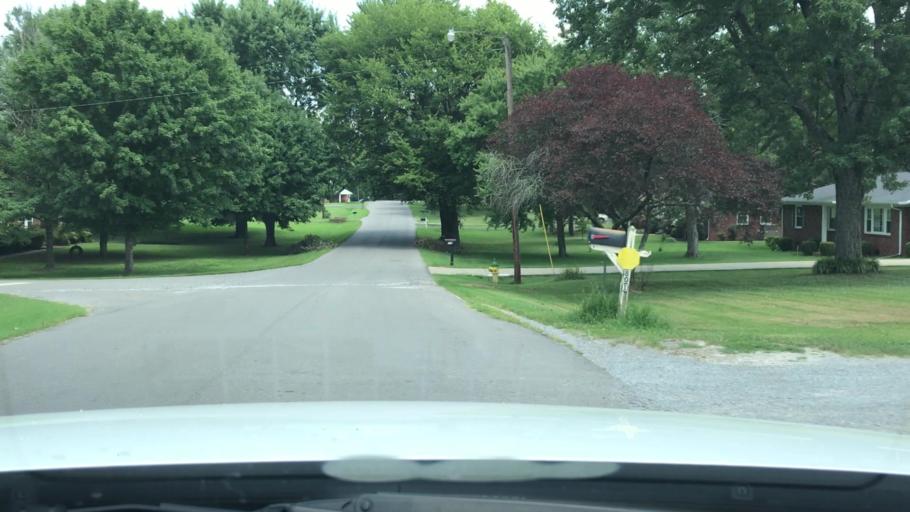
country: US
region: Tennessee
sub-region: Sumner County
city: Gallatin
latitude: 36.3734
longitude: -86.4694
